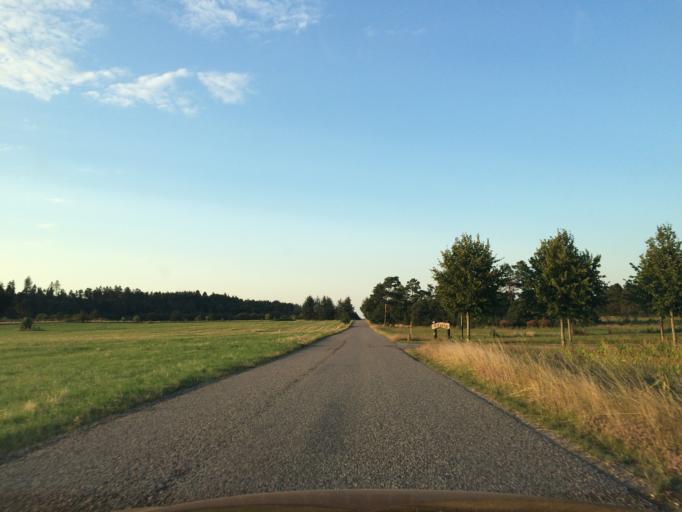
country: DK
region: Central Jutland
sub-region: Silkeborg Kommune
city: Svejbaek
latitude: 56.1863
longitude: 9.6417
